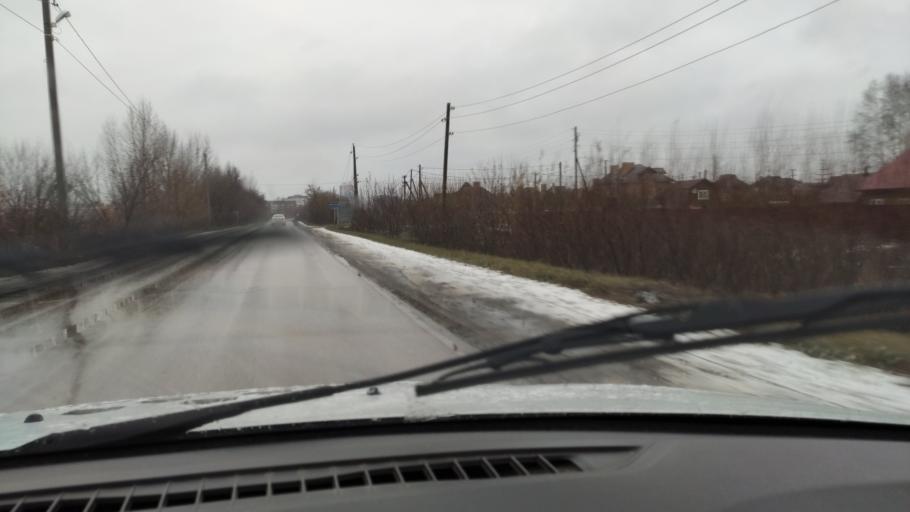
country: RU
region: Perm
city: Kondratovo
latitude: 57.9680
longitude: 56.1170
